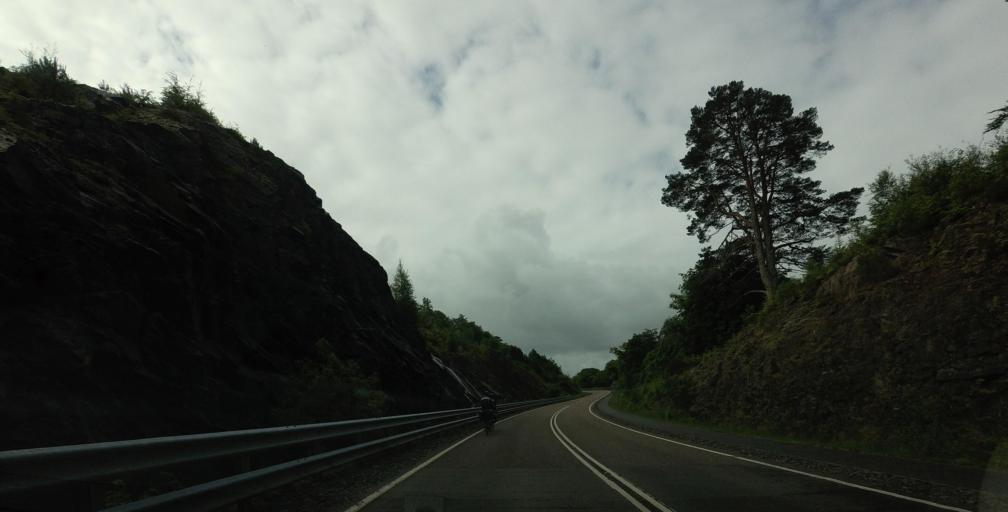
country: GB
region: Scotland
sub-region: Argyll and Bute
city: Isle Of Mull
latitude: 56.9113
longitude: -5.8216
